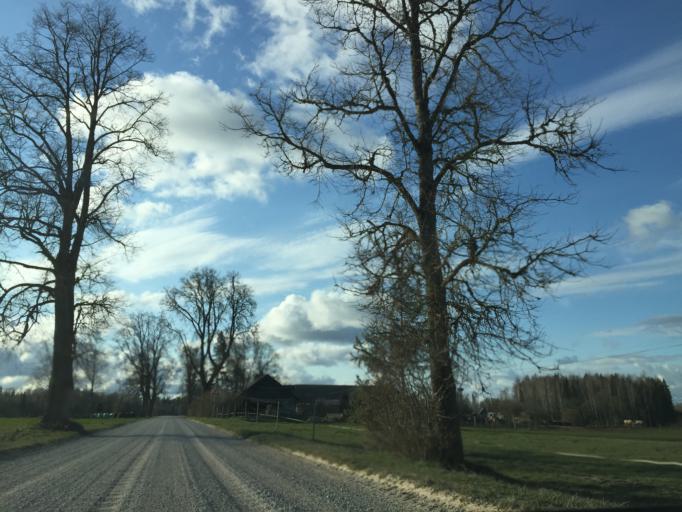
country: LV
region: Burtnieki
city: Matisi
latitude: 57.6035
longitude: 25.0828
